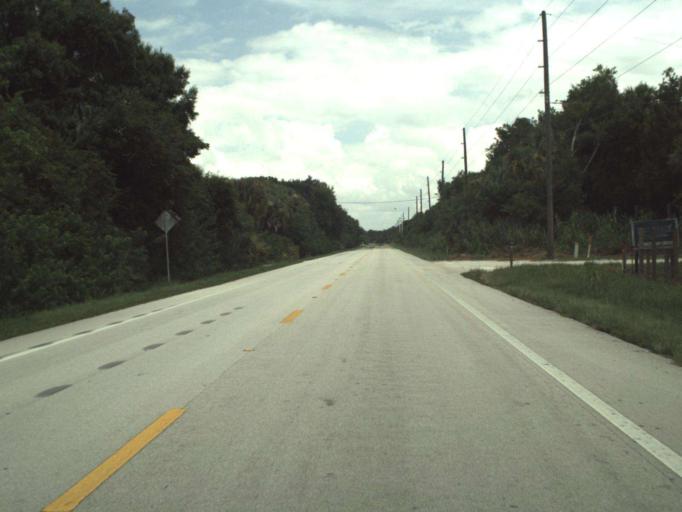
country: US
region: Florida
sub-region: Okeechobee County
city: Taylor Creek
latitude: 27.1028
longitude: -80.6590
